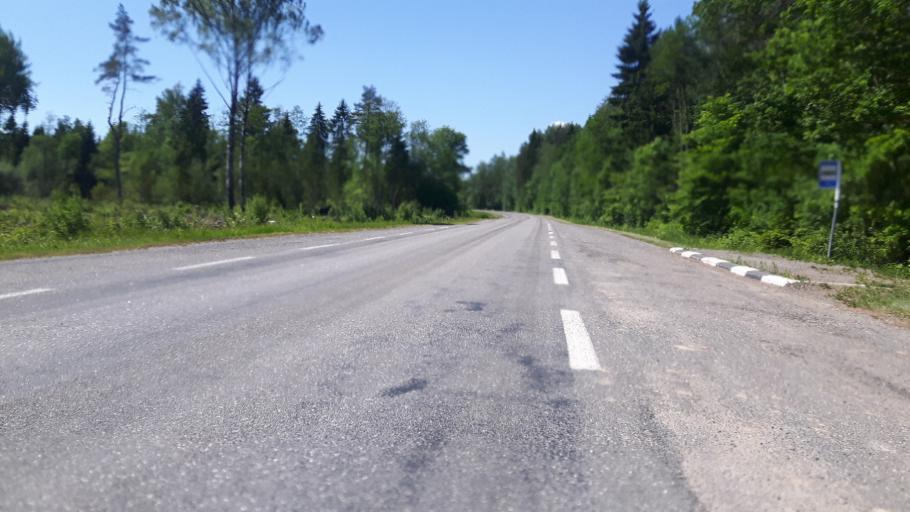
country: EE
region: Paernumaa
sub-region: Tootsi vald
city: Tootsi
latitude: 58.4981
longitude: 24.8574
